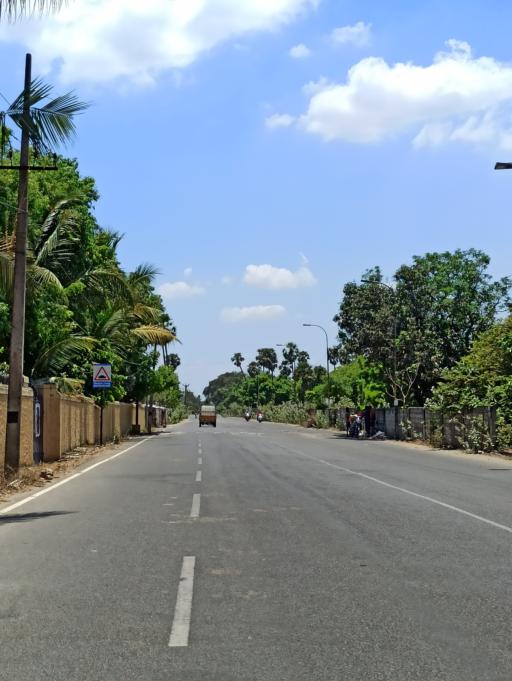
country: IN
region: Tamil Nadu
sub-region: Thiruvallur
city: Chinnasekkadu
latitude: 13.1566
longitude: 80.2372
